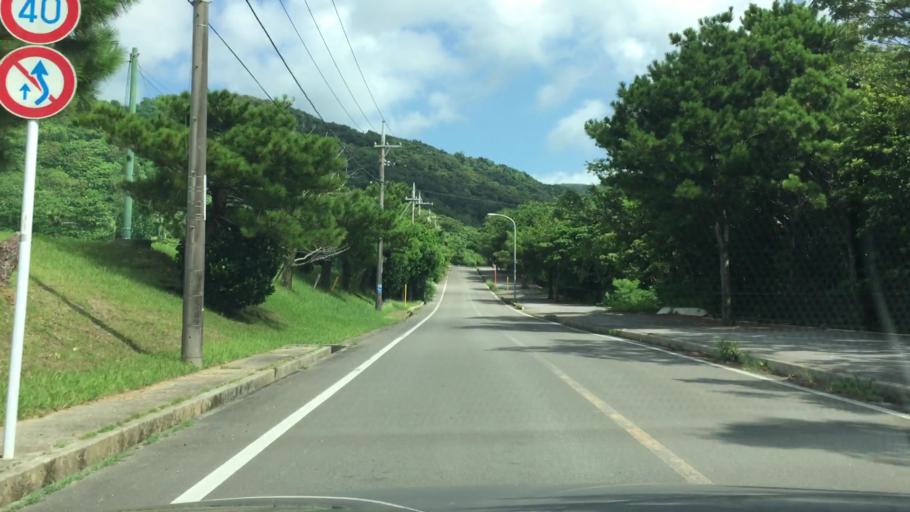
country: JP
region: Okinawa
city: Ishigaki
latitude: 24.4247
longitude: 124.2124
